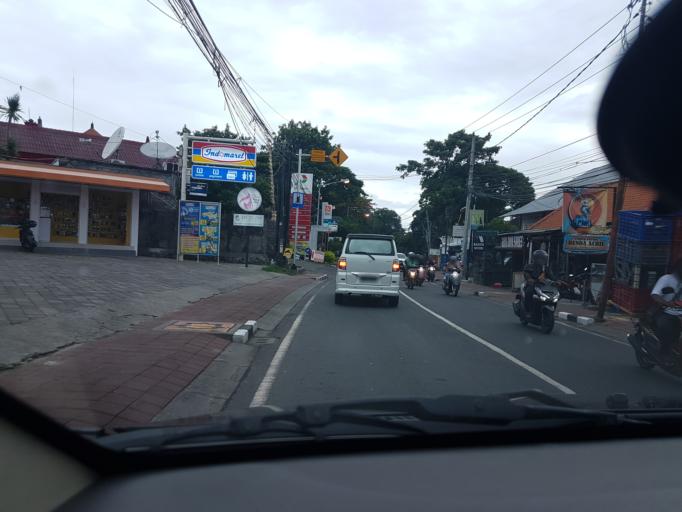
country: ID
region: Bali
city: Banjar Gunungpande
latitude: -8.6382
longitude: 115.1742
